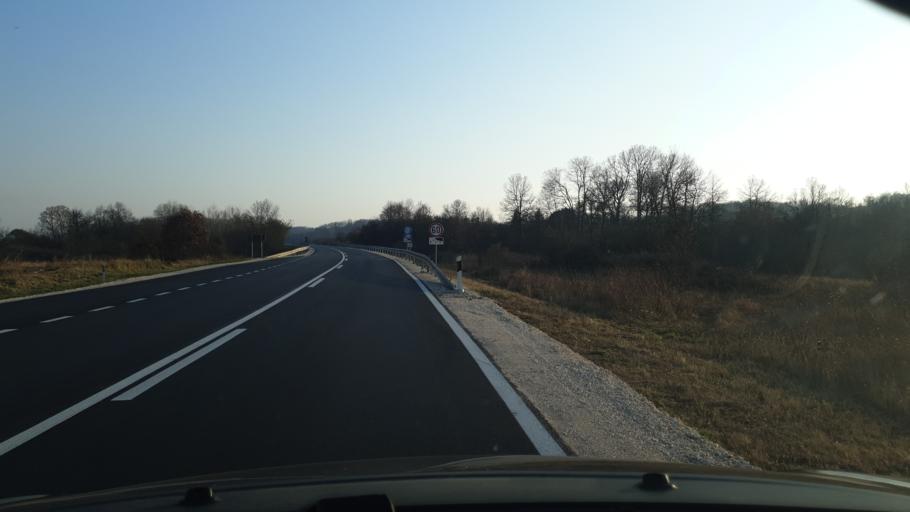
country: RS
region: Central Serbia
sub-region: Zajecarski Okrug
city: Zajecar
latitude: 43.9765
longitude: 22.2914
